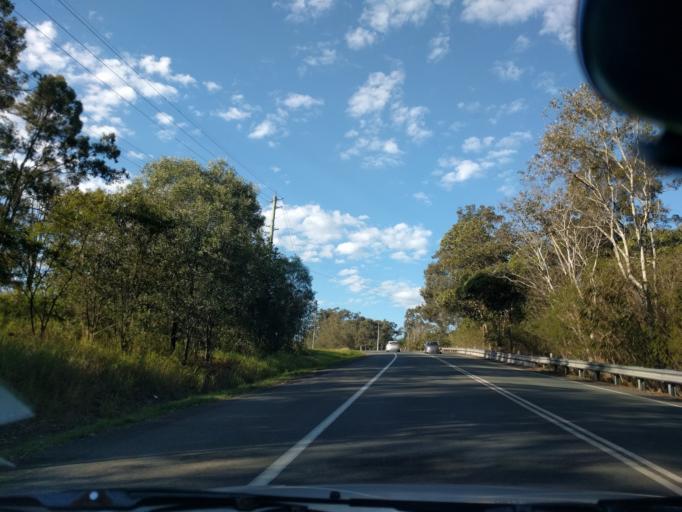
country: AU
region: Queensland
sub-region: Brisbane
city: Pullenvale
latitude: -27.5419
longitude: 152.8924
